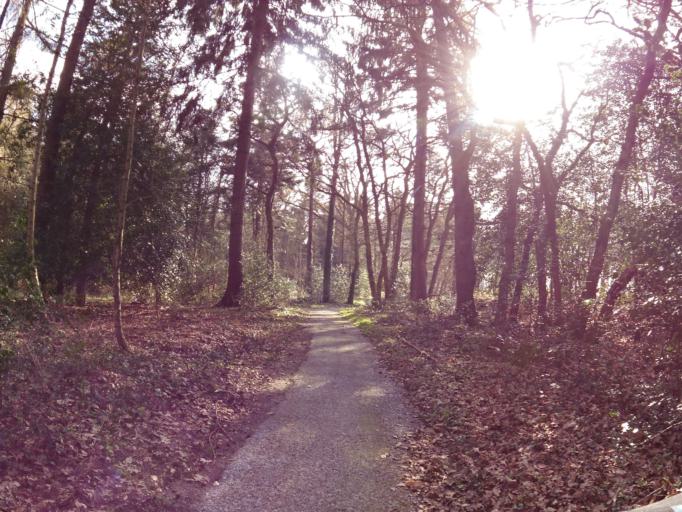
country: NL
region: Overijssel
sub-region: Gemeente Steenwijkerland
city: Tuk
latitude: 52.8195
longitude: 6.1122
